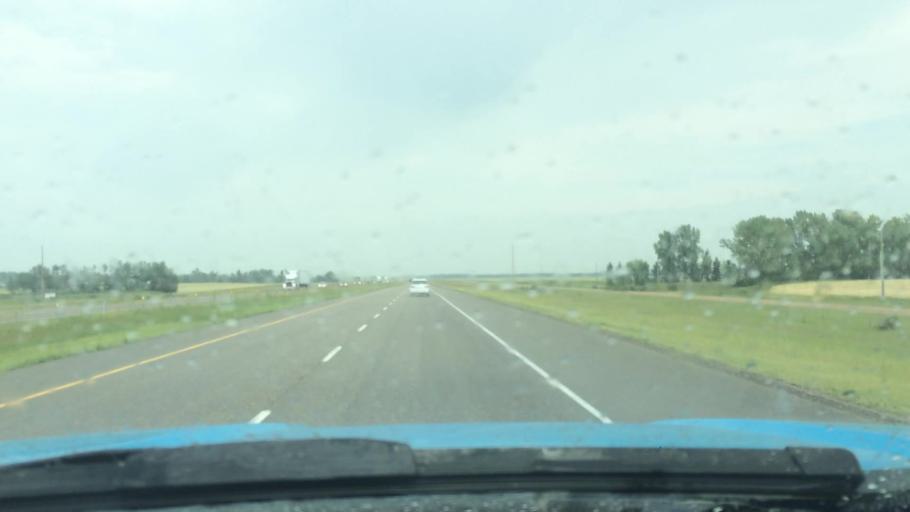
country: CA
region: Alberta
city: Olds
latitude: 51.7196
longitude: -114.0254
